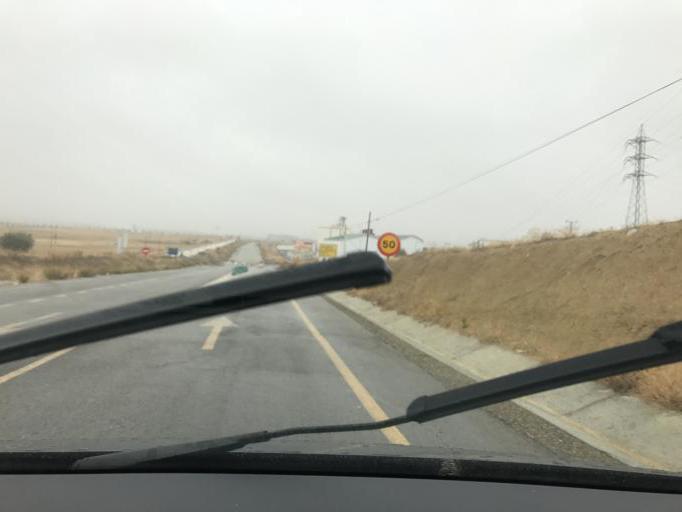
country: ES
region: Andalusia
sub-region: Provincia de Granada
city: Escuzar
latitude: 37.0879
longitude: -3.7490
